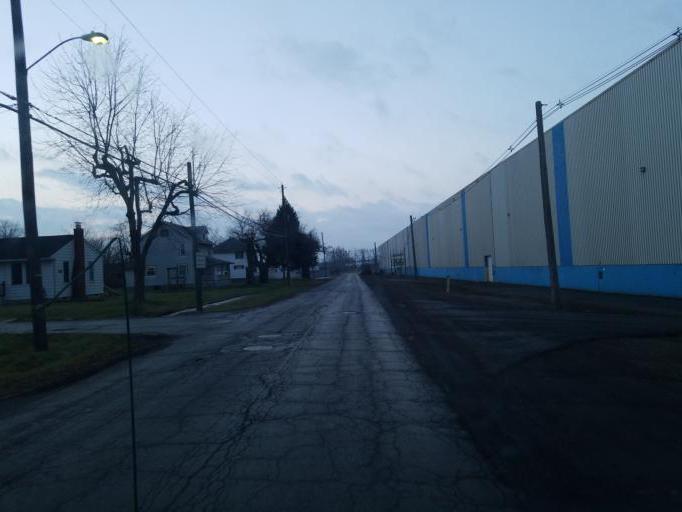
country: US
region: Ohio
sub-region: Marion County
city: Marion
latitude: 40.5674
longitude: -83.1409
